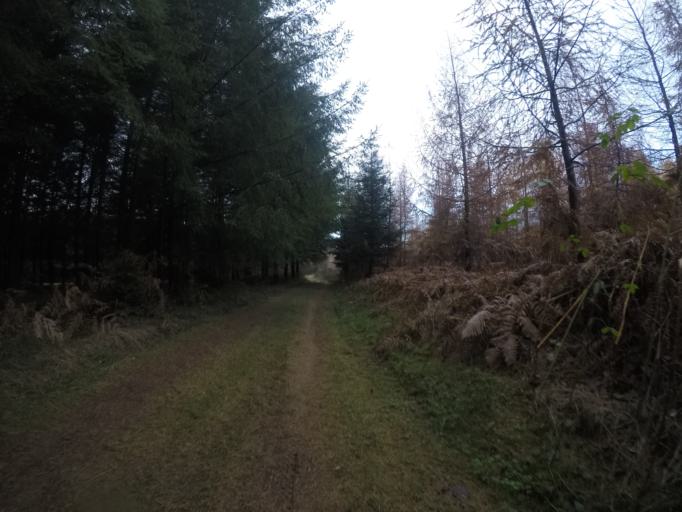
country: BE
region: Wallonia
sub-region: Province du Luxembourg
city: Habay-la-Vieille
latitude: 49.7403
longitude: 5.6037
